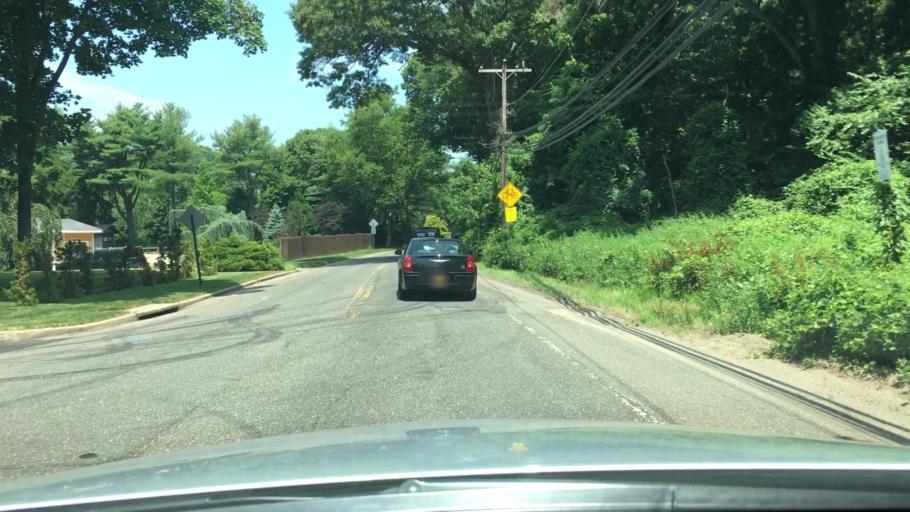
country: US
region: New York
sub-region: Suffolk County
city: West Hills
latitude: 40.8139
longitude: -73.4440
